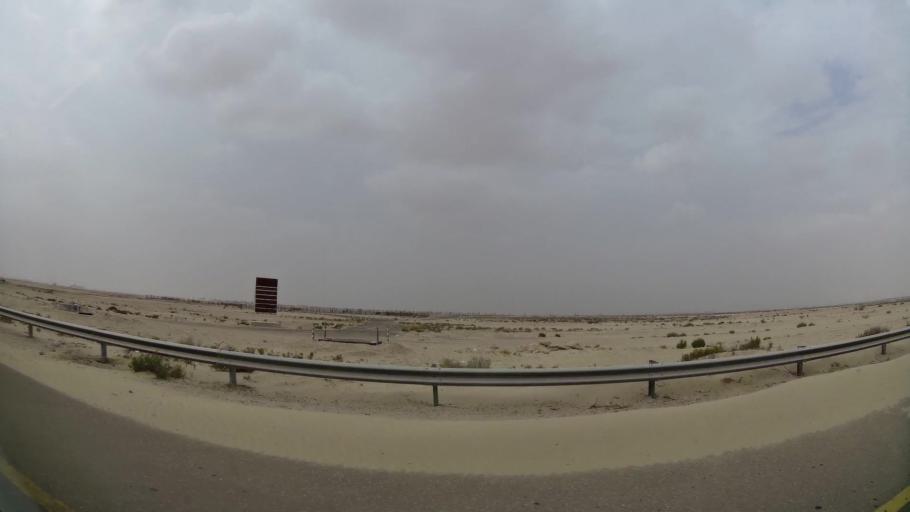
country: AE
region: Abu Dhabi
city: Abu Dhabi
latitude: 24.3899
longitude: 54.6810
